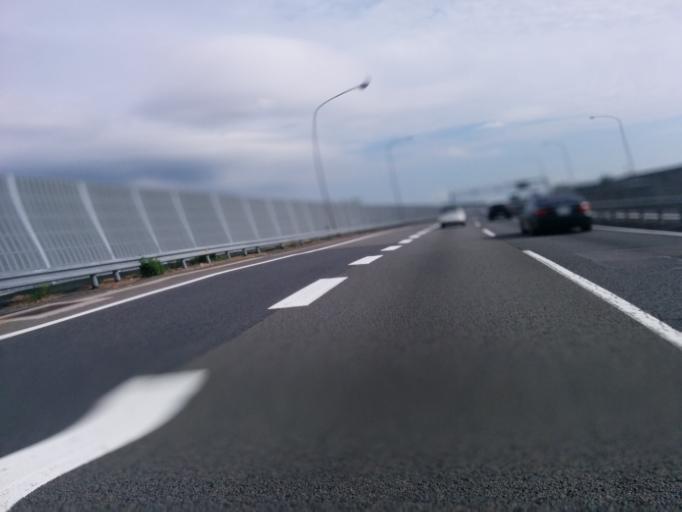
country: JP
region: Mie
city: Komono
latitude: 34.9334
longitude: 136.4887
